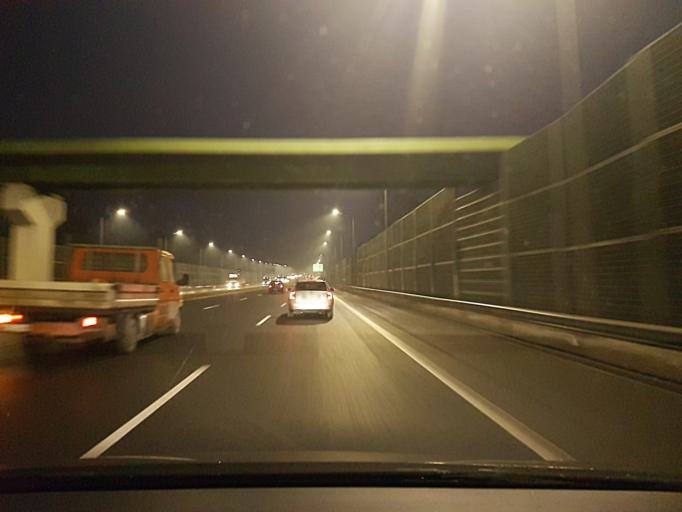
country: PL
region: Masovian Voivodeship
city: Zielonka
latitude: 52.3178
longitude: 21.1360
